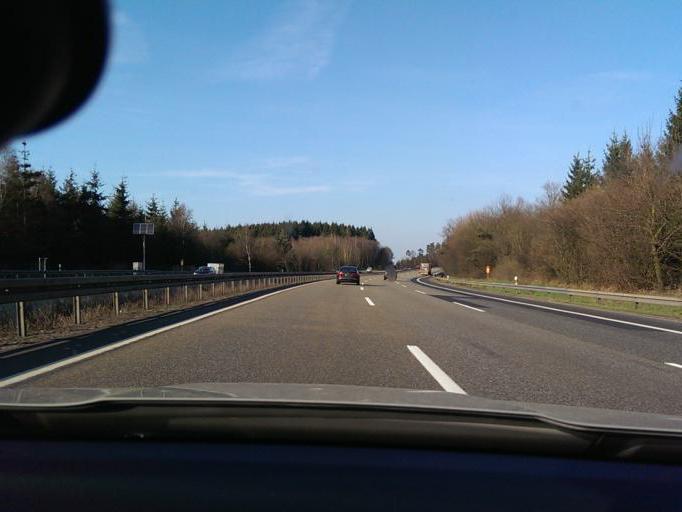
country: DE
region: Hesse
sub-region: Regierungsbezirk Kassel
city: Kirchheim
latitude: 50.8709
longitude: 9.5954
